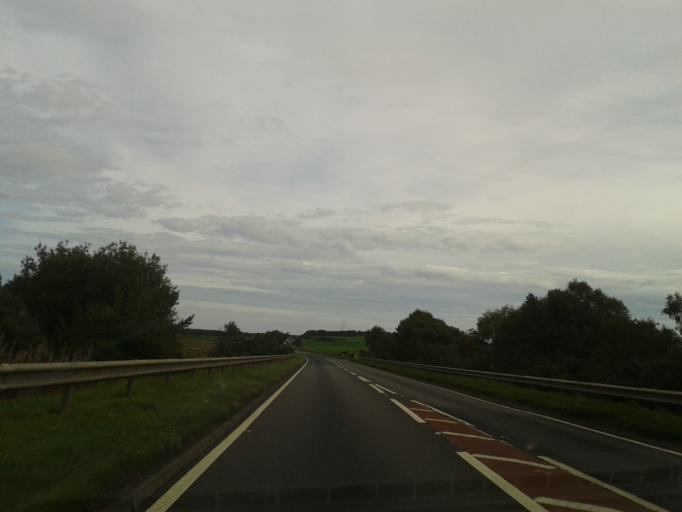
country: GB
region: Scotland
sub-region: Highland
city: Nairn
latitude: 57.5567
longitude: -3.9712
